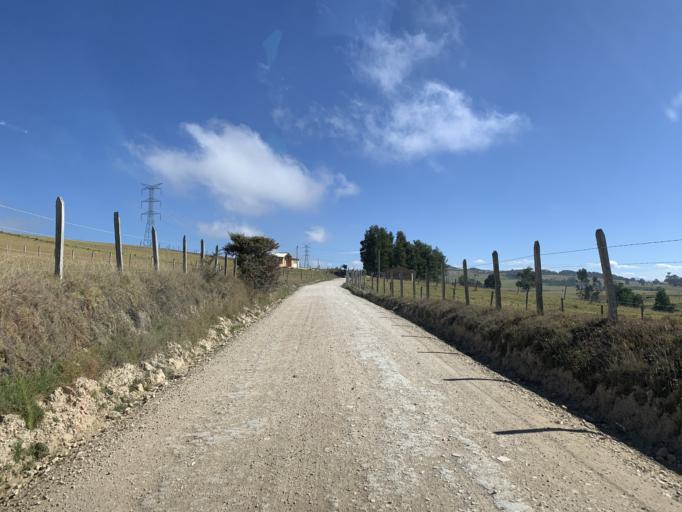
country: CO
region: Boyaca
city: Tuta
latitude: 5.6697
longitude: -73.1493
